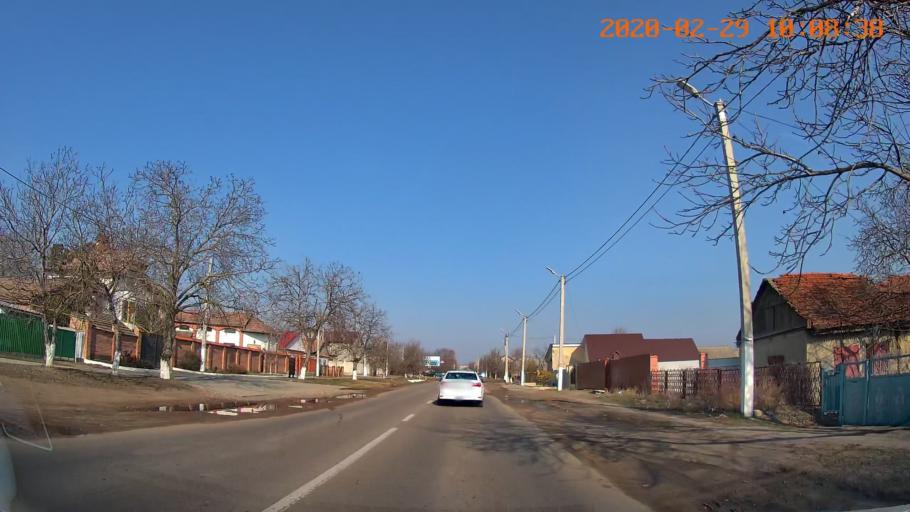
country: MD
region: Telenesti
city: Tiraspolul Nou
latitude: 46.8234
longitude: 29.6562
